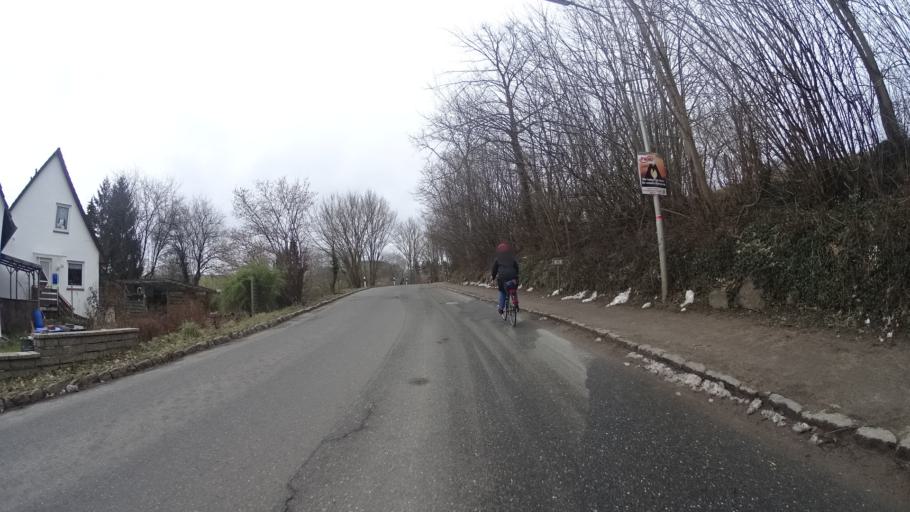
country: DE
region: Schleswig-Holstein
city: Neukirchen
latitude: 54.2123
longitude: 10.5547
